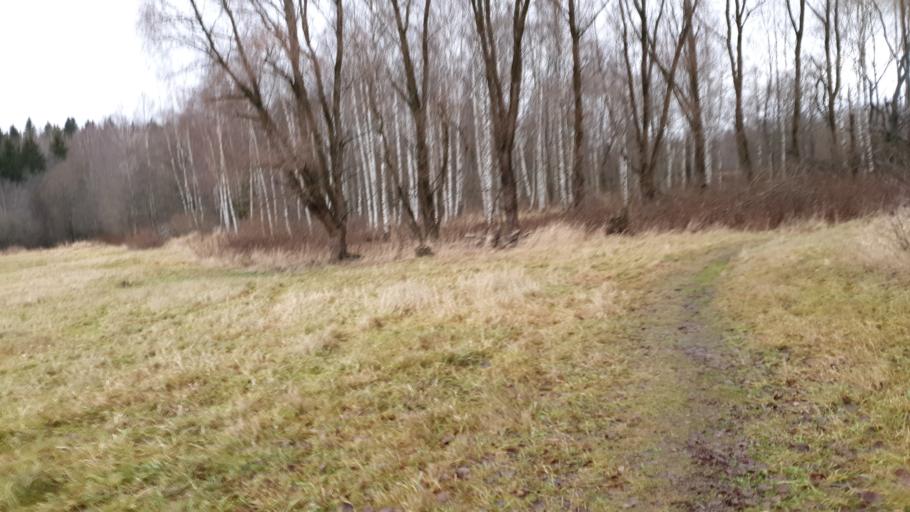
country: FI
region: Uusimaa
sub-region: Helsinki
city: Teekkarikylae
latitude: 60.2691
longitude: 24.8637
